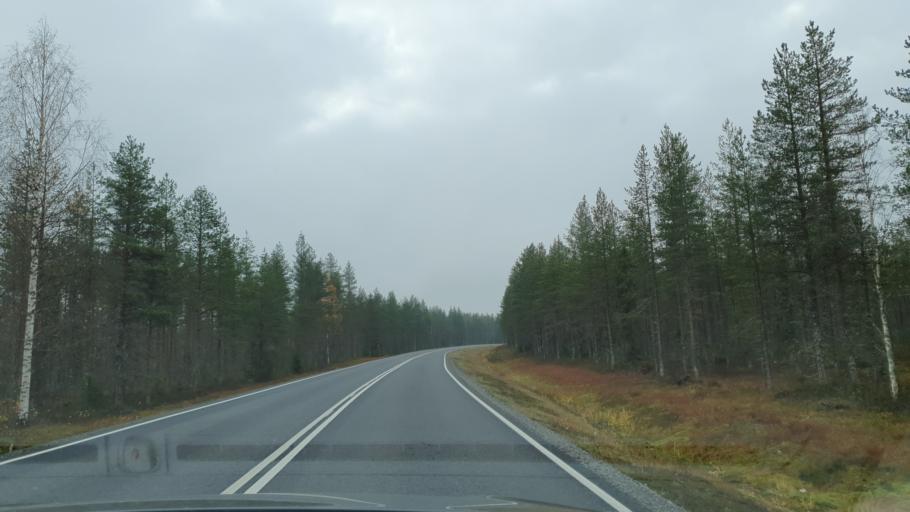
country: FI
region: Lapland
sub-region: Rovaniemi
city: Ranua
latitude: 66.0576
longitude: 26.3685
